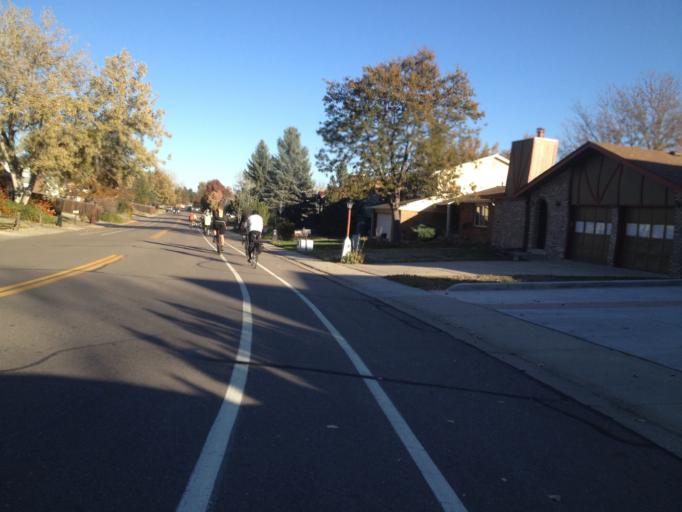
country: US
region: Colorado
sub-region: Boulder County
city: Longmont
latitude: 40.1853
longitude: -105.1379
